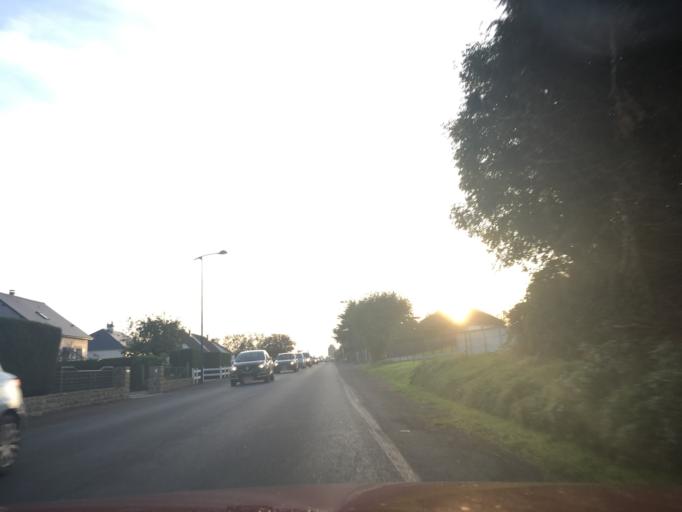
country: FR
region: Lower Normandy
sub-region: Departement de la Manche
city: Avranches
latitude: 48.7016
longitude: -1.3543
